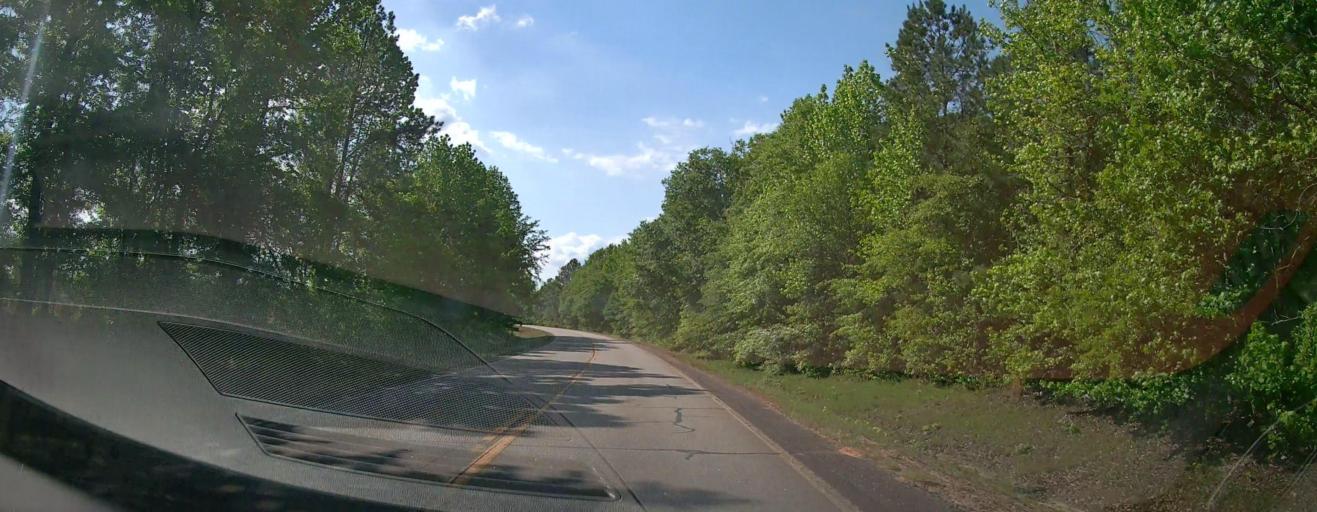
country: US
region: Georgia
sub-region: Washington County
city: Tennille
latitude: 32.9074
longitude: -82.9740
